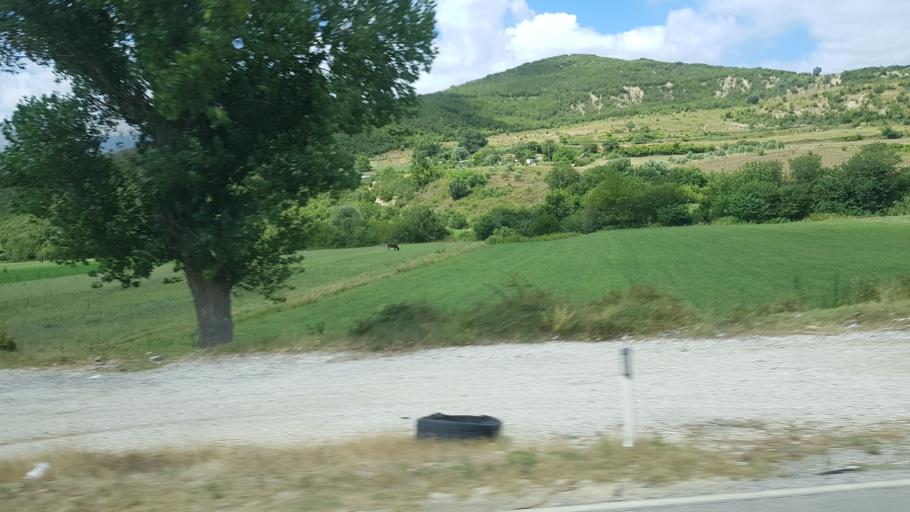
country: AL
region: Gjirokaster
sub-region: Rrethi i Tepelenes
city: Krahes
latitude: 40.4151
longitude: 19.8585
